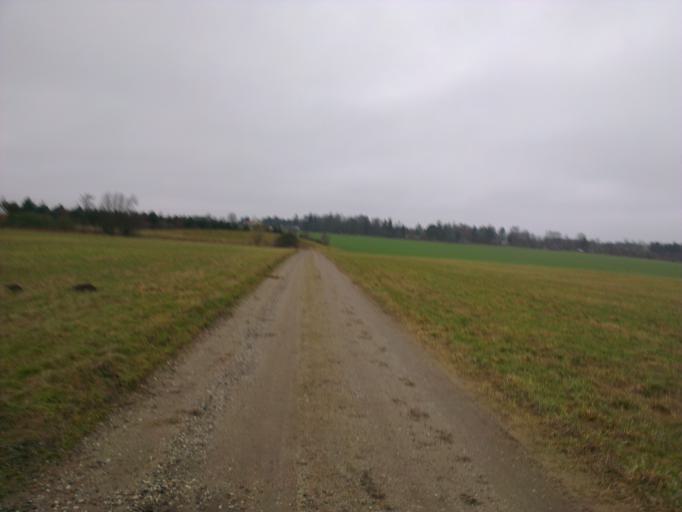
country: DK
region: Capital Region
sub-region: Frederikssund Kommune
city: Jaegerspris
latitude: 55.8440
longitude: 12.0052
